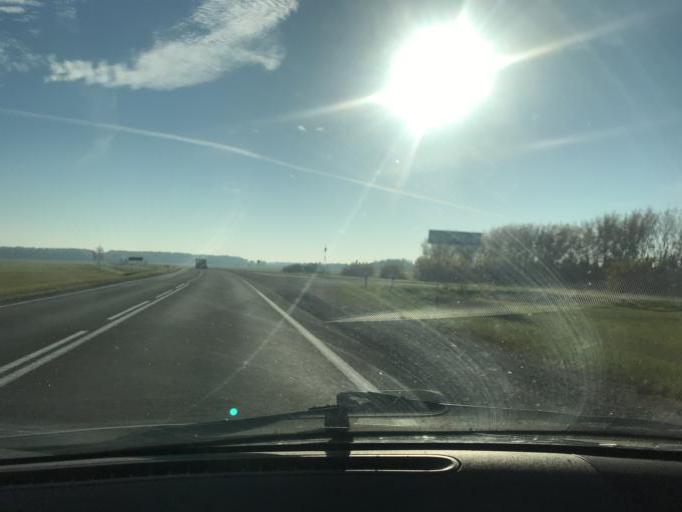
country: BY
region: Brest
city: Drahichyn
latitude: 52.1559
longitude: 25.3356
